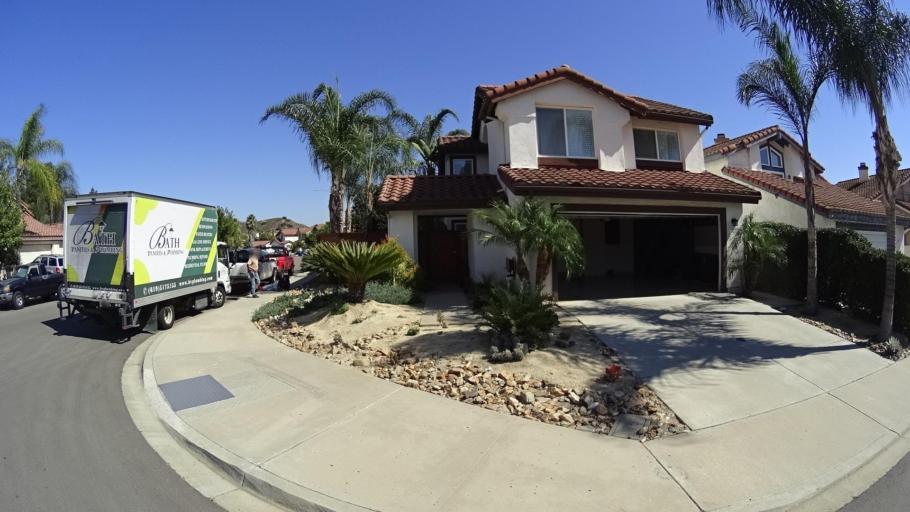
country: US
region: California
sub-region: San Diego County
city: Rancho San Diego
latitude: 32.7501
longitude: -116.9375
